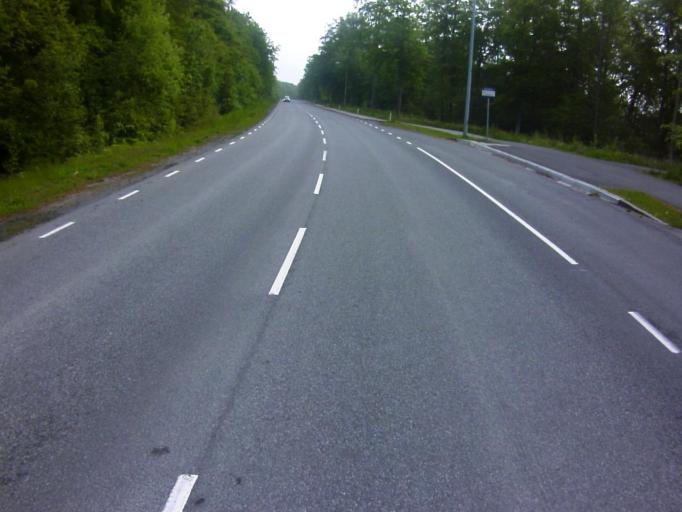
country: SE
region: Blekinge
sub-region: Solvesborgs Kommun
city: Soelvesborg
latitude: 56.0545
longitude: 14.5702
